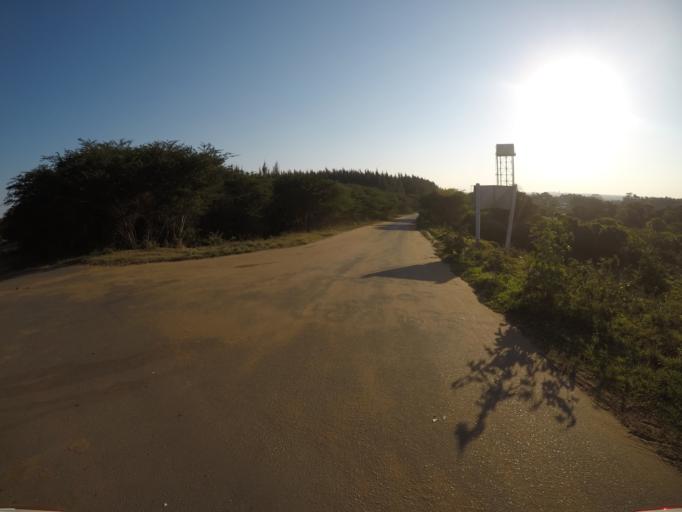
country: ZA
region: KwaZulu-Natal
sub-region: uThungulu District Municipality
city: KwaMbonambi
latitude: -28.7083
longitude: 32.1840
